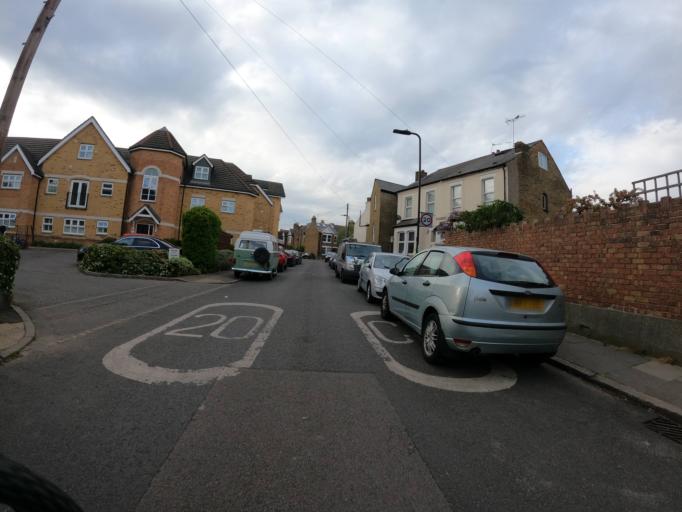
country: GB
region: England
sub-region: Greater London
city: Isleworth
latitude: 51.5026
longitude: -0.3384
